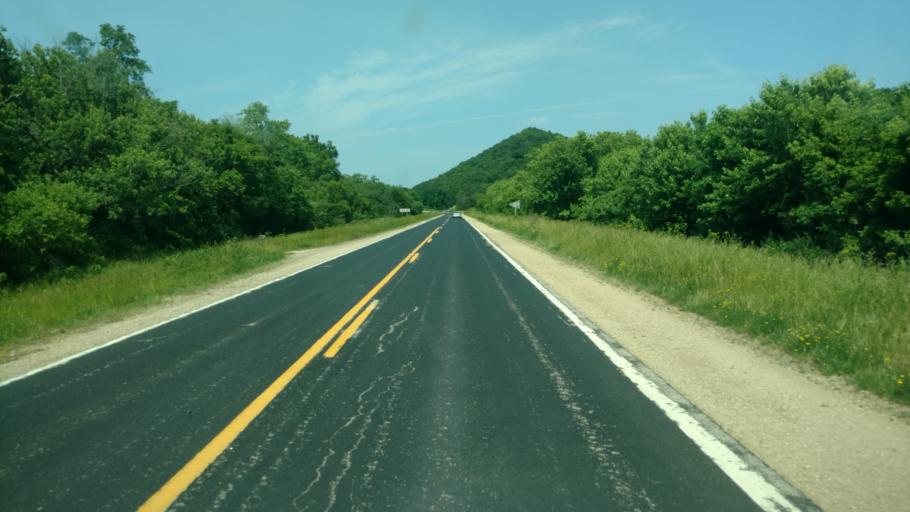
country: US
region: Wisconsin
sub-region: Monroe County
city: Cashton
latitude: 43.5583
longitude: -90.6460
